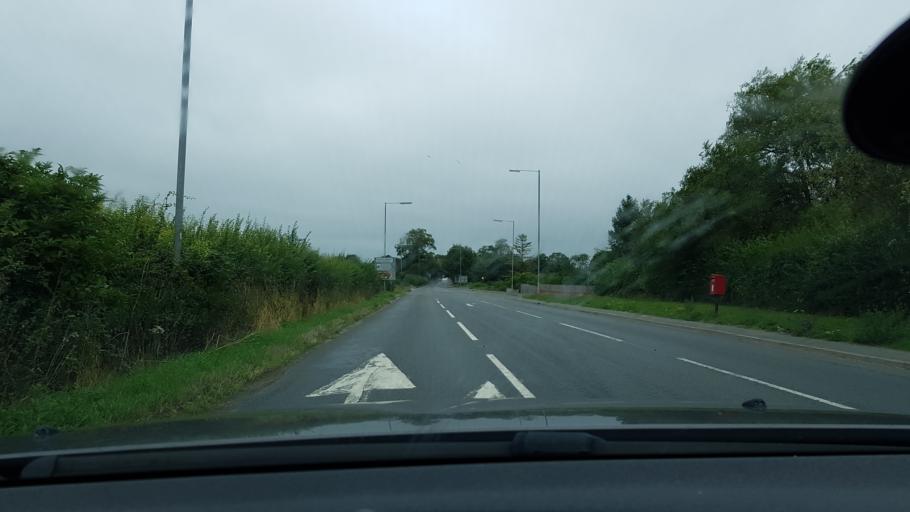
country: GB
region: England
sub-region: Wiltshire
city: Calne
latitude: 51.4272
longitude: -1.9697
